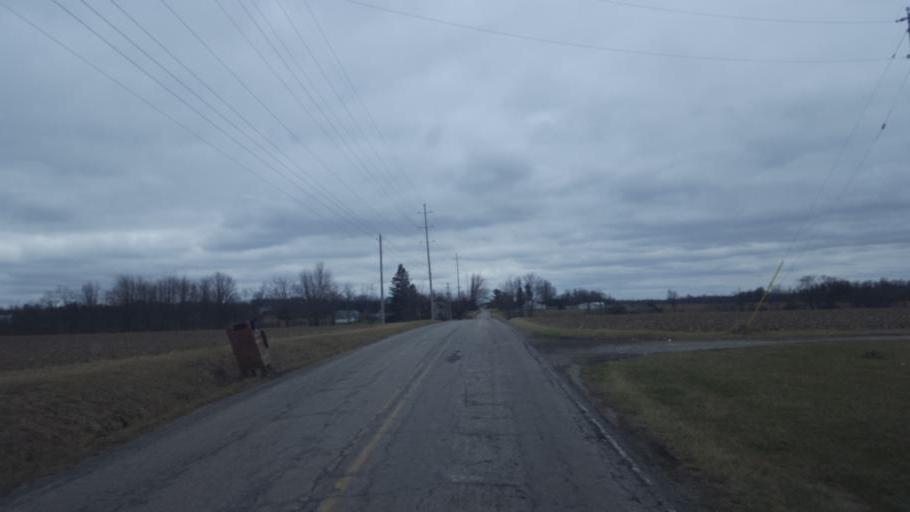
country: US
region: Ohio
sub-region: Crawford County
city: Crestline
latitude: 40.7749
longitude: -82.6980
